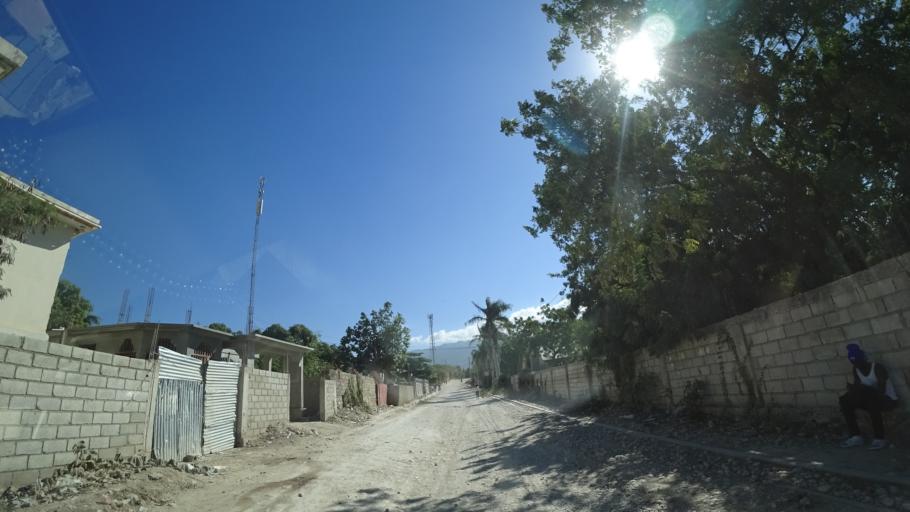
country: HT
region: Ouest
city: Delmas 73
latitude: 18.5489
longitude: -72.2873
